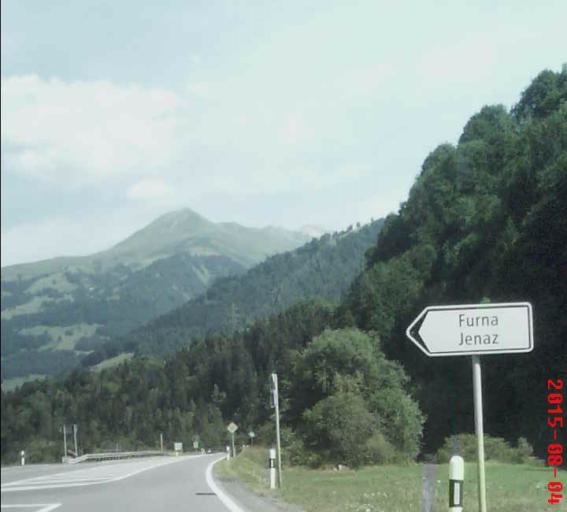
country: CH
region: Grisons
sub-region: Praettigau/Davos District
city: Jenaz
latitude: 46.9361
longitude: 9.7118
